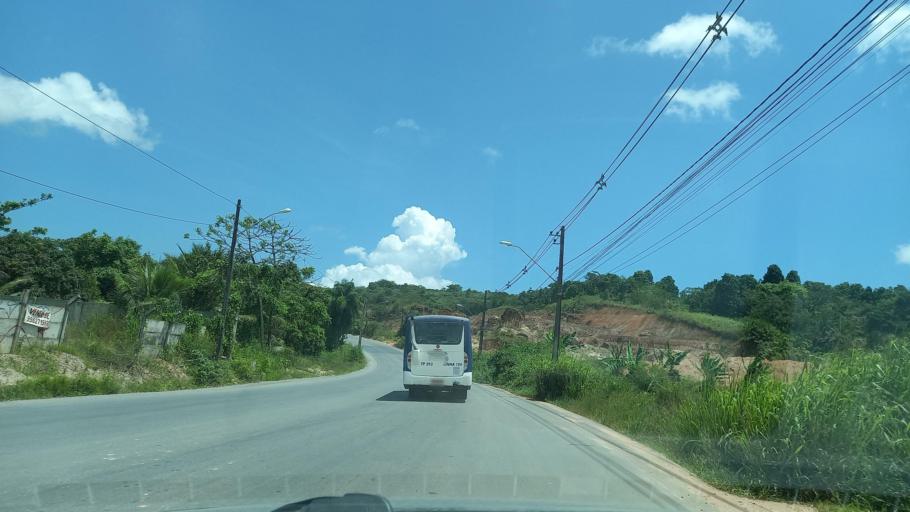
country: BR
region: Pernambuco
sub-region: Jaboatao Dos Guararapes
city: Jaboatao
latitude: -8.1620
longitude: -34.9910
